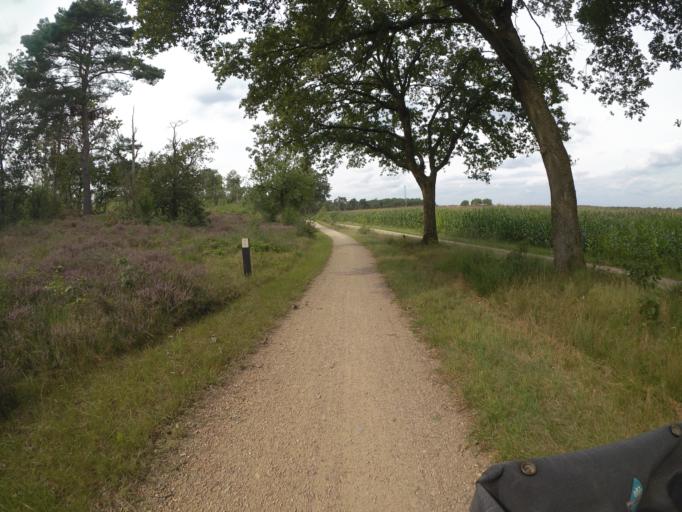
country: NL
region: Limburg
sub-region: Gemeente Bergen
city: Wellerlooi
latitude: 51.5522
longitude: 6.1484
